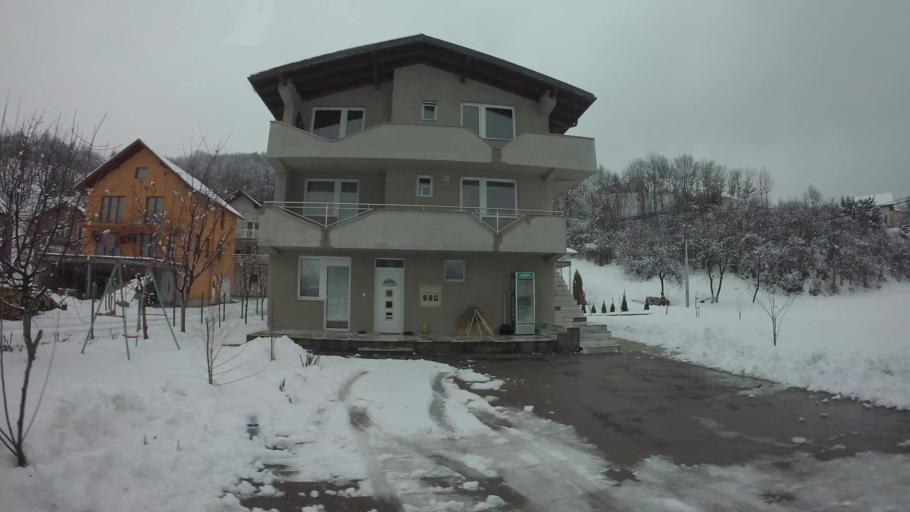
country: BA
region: Federation of Bosnia and Herzegovina
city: Hadzici
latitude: 43.8500
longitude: 18.2521
